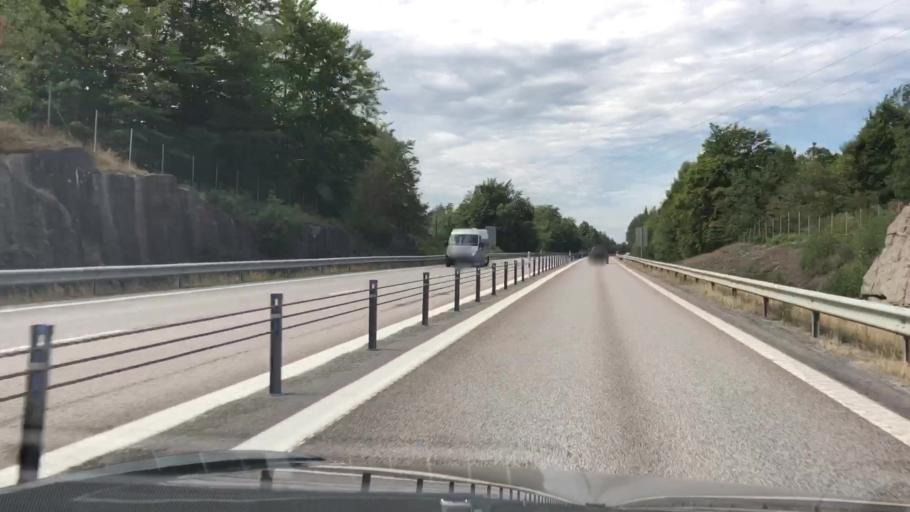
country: SE
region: Blekinge
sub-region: Ronneby Kommun
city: Brakne-Hoby
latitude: 56.2174
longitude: 15.1840
